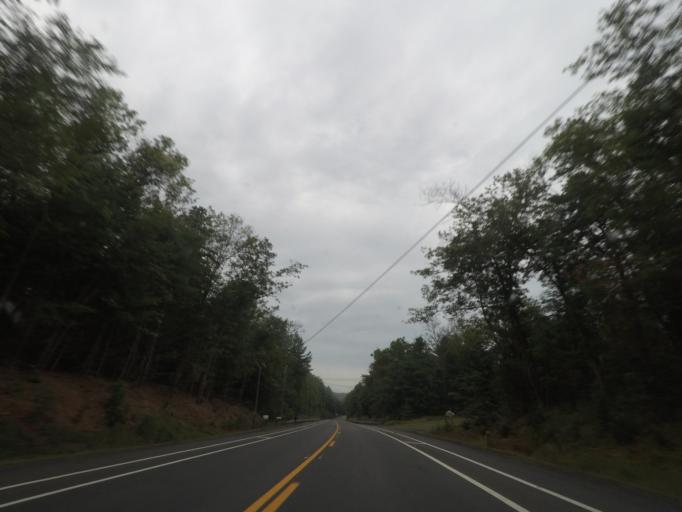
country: US
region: Massachusetts
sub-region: Hampden County
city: Palmer
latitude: 42.1712
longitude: -72.2643
